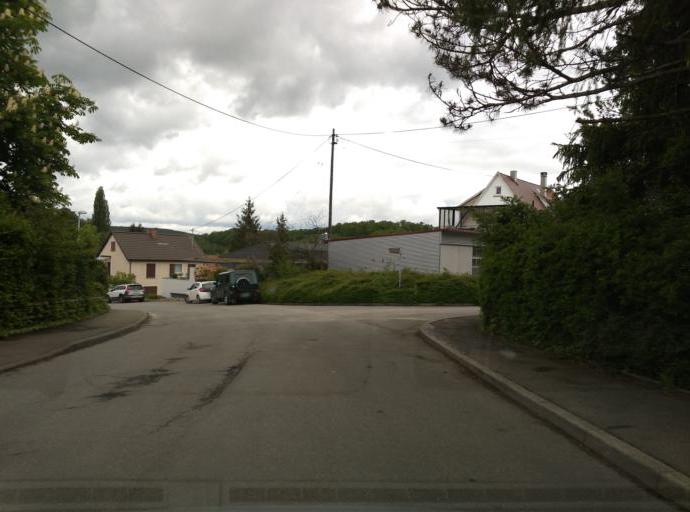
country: DE
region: Baden-Wuerttemberg
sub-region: Tuebingen Region
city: Wannweil
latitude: 48.5135
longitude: 9.1474
